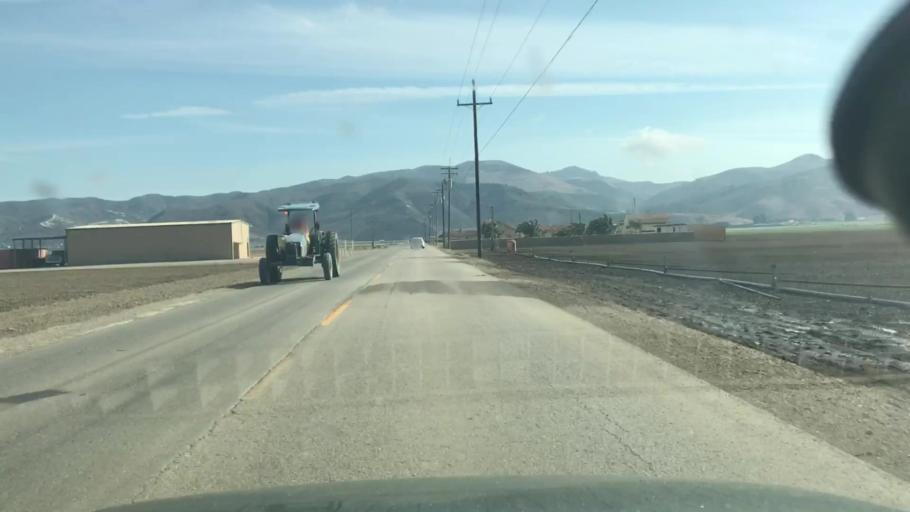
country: US
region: California
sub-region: Santa Barbara County
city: Lompoc
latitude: 34.6561
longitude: -120.4930
